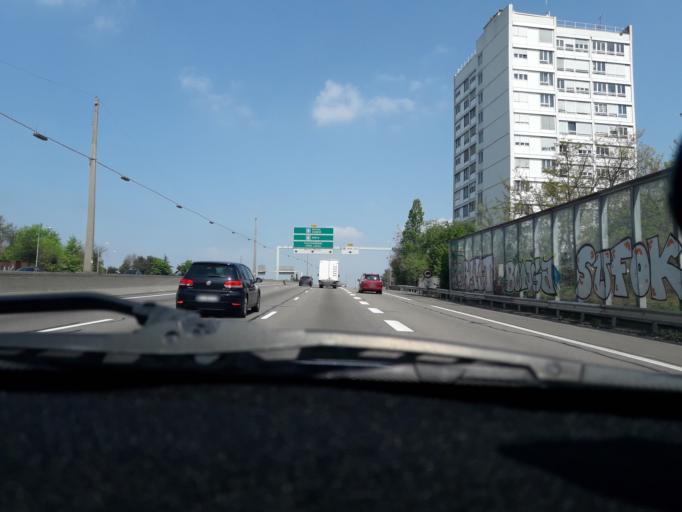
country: FR
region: Rhone-Alpes
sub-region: Departement du Rhone
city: Bron
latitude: 45.7326
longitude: 4.9005
